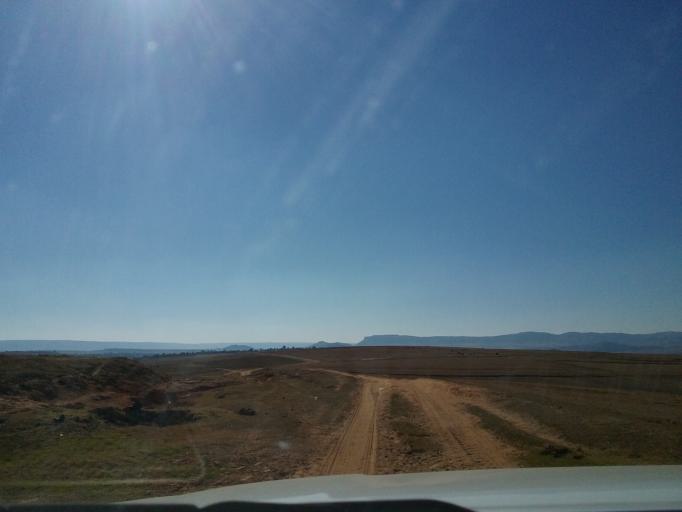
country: LS
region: Maseru
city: Nako
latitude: -29.4970
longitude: 27.5981
